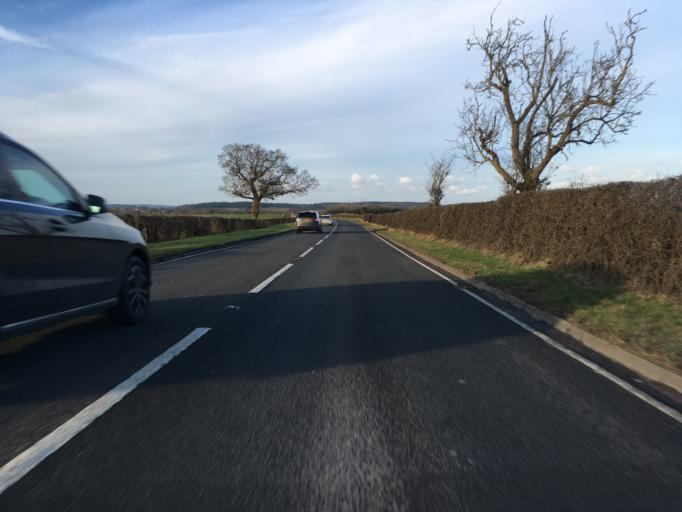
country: GB
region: England
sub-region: Warwickshire
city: Stratford-upon-Avon
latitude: 52.2337
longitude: -1.7418
